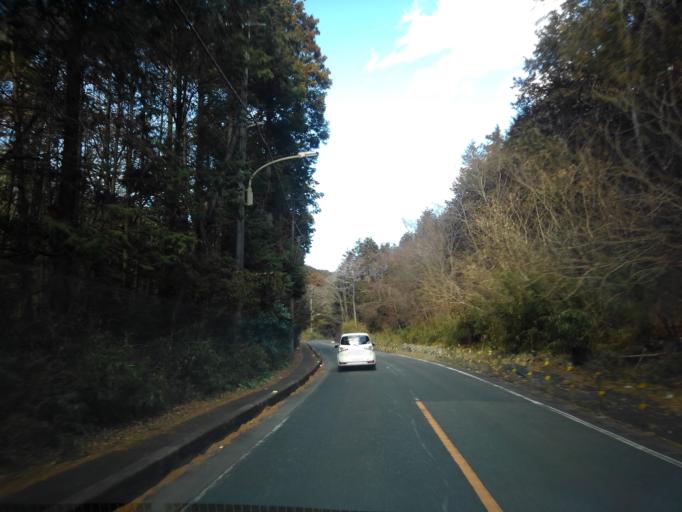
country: JP
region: Saitama
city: Hanno
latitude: 35.8252
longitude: 139.3395
